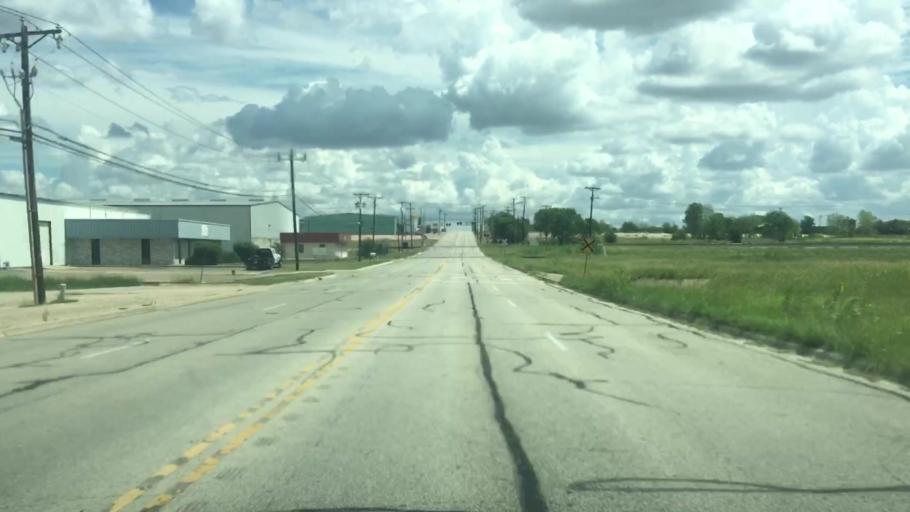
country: US
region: Texas
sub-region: Bell County
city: Temple
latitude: 31.1292
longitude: -97.3514
